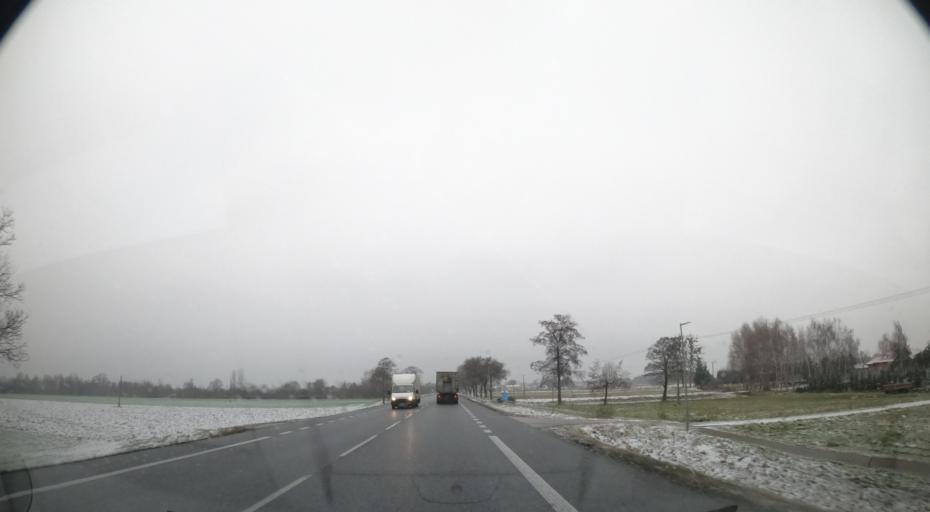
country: PL
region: Masovian Voivodeship
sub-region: Powiat sochaczewski
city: Teresin
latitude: 52.2196
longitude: 20.3462
